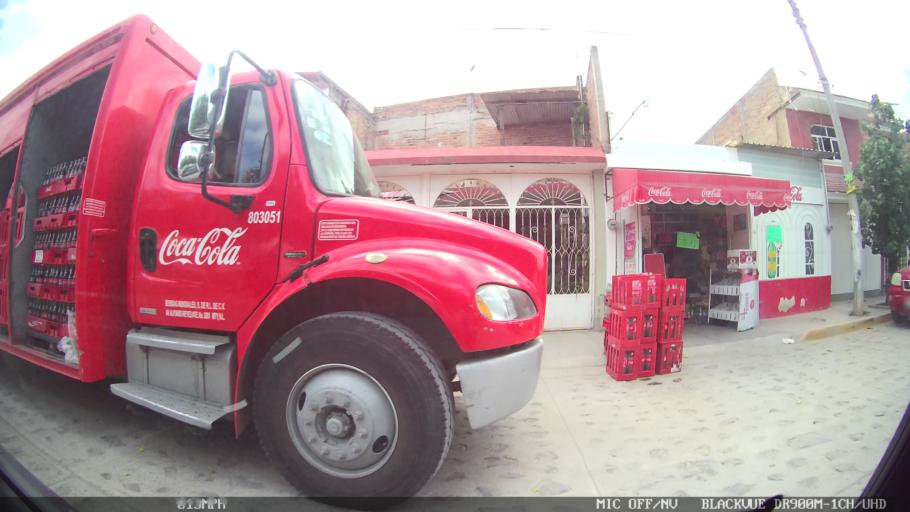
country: MX
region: Jalisco
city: Tlaquepaque
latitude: 20.6722
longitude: -103.2553
